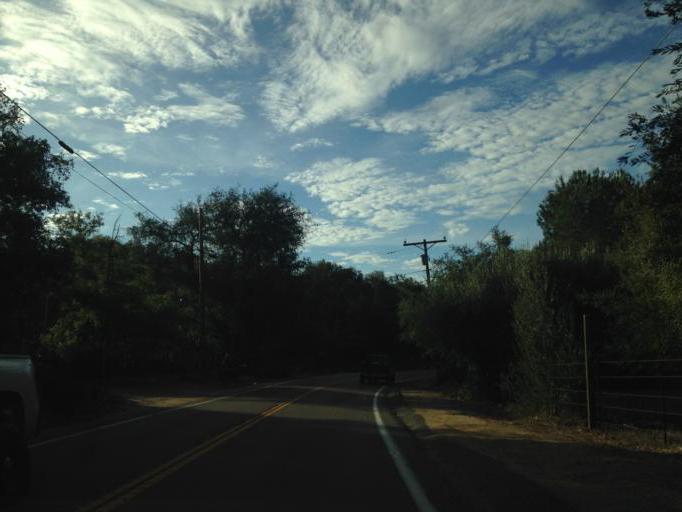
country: US
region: California
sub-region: San Diego County
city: Rainbow
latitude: 33.4267
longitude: -117.0889
